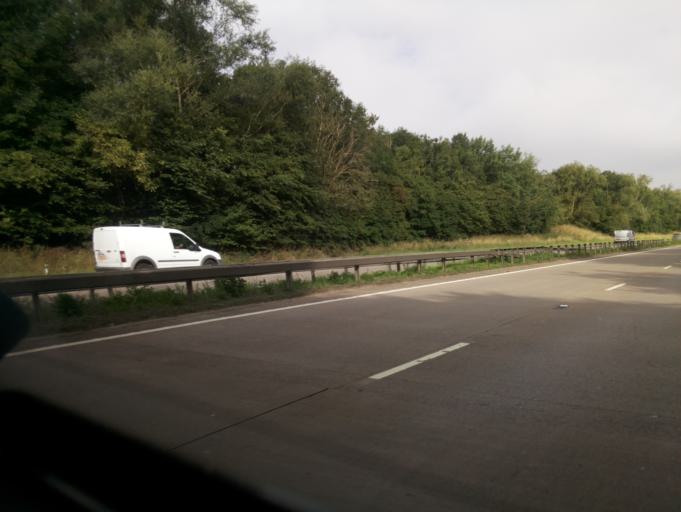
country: GB
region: England
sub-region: Wiltshire
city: Cricklade
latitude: 51.6644
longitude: -1.8857
